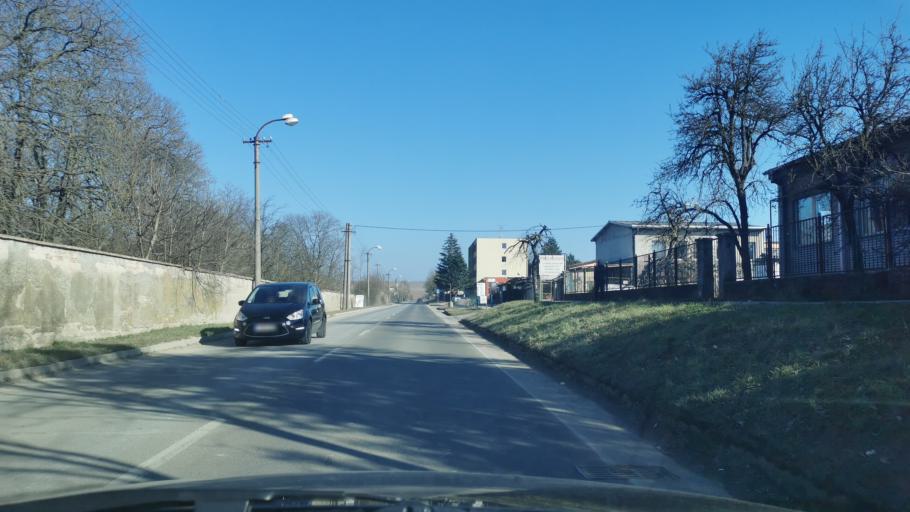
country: SK
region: Trnavsky
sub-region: Okres Senica
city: Senica
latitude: 48.6815
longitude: 17.3804
